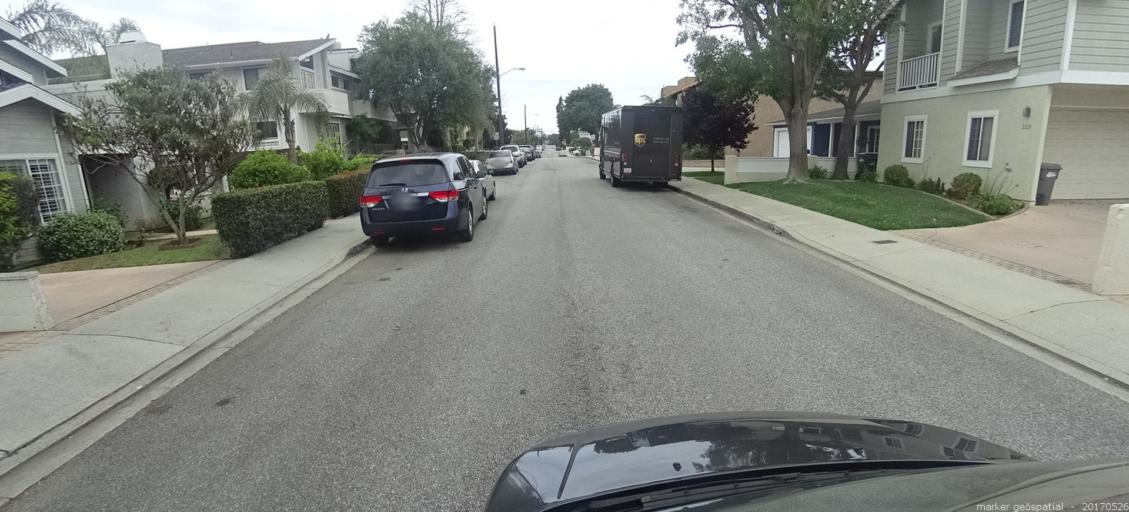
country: US
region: California
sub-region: Los Angeles County
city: Lawndale
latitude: 33.8747
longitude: -118.3708
